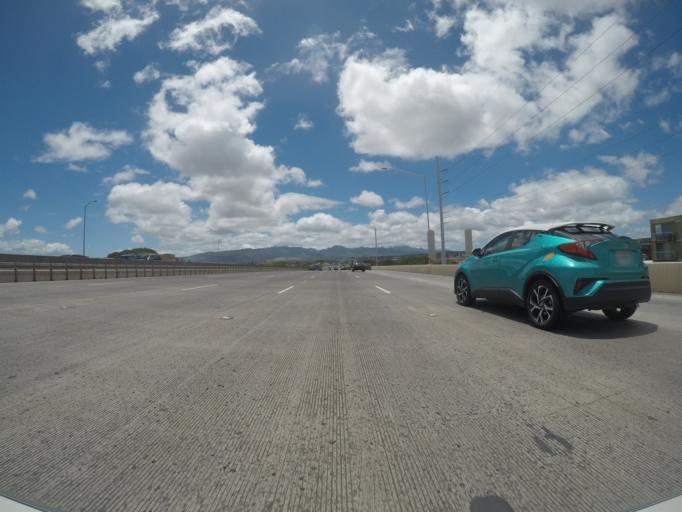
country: US
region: Hawaii
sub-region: Honolulu County
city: Pearl City, Manana
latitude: 21.3909
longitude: -157.9718
